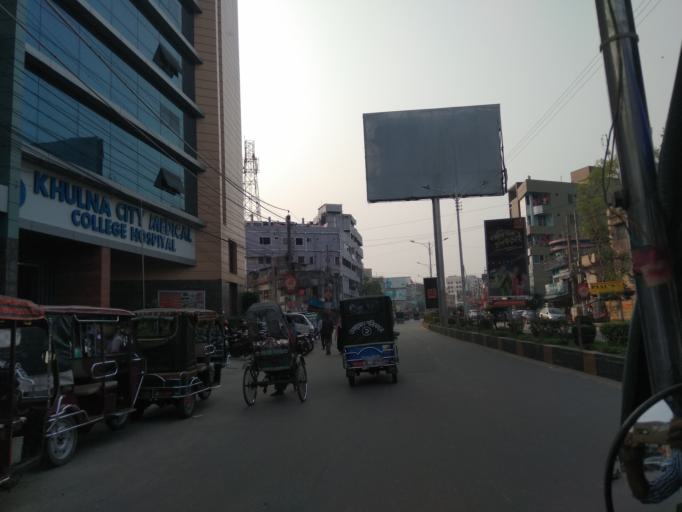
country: BD
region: Khulna
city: Khulna
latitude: 22.8132
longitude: 89.5566
